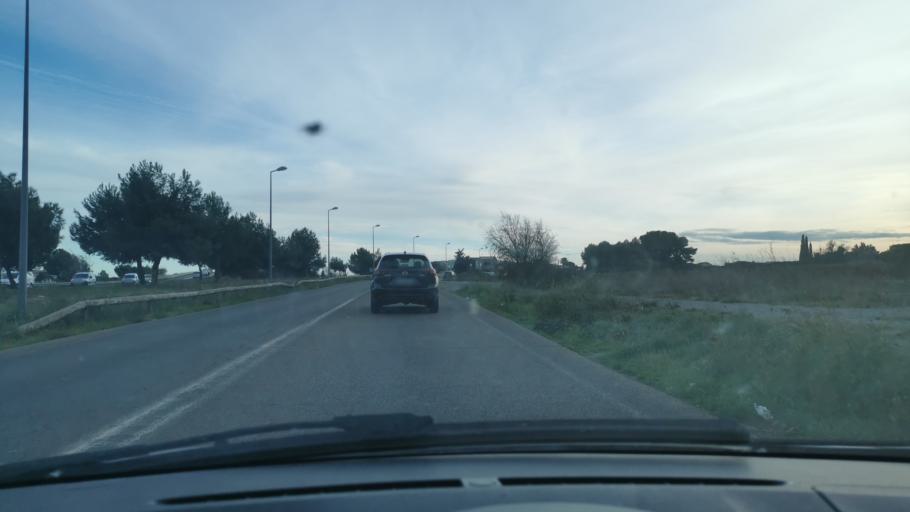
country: FR
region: Languedoc-Roussillon
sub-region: Departement de l'Herault
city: Frontignan
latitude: 43.4651
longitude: 3.7661
